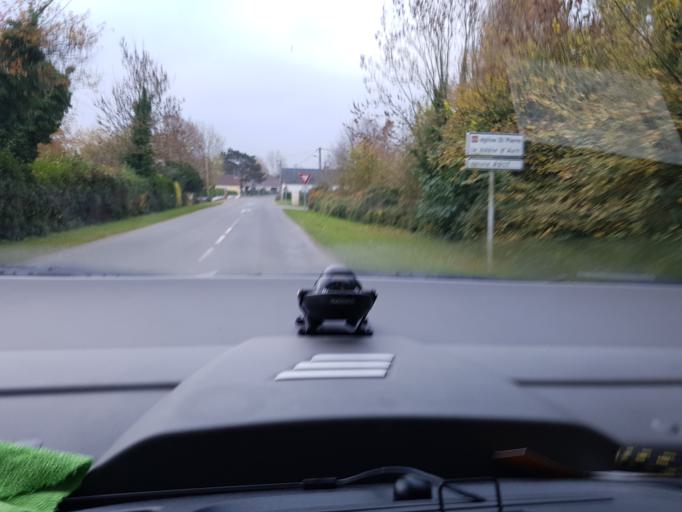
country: FR
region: Picardie
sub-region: Departement de la Somme
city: Cayeux-sur-Mer
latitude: 50.1406
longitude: 1.5184
